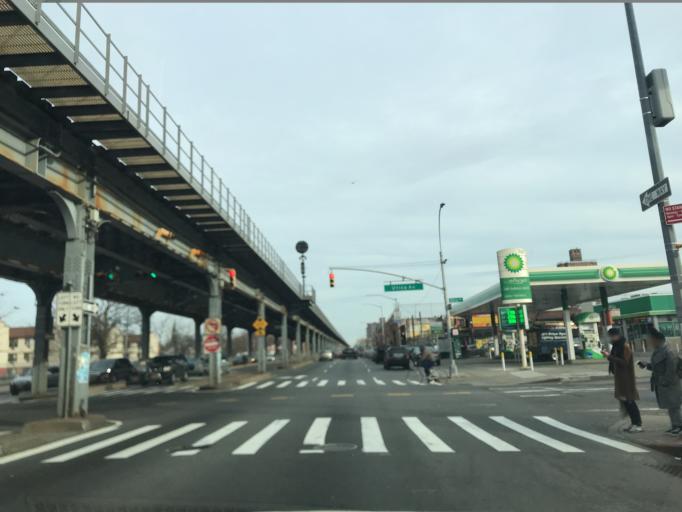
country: US
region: New York
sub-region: Kings County
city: Brooklyn
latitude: 40.6773
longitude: -73.9306
